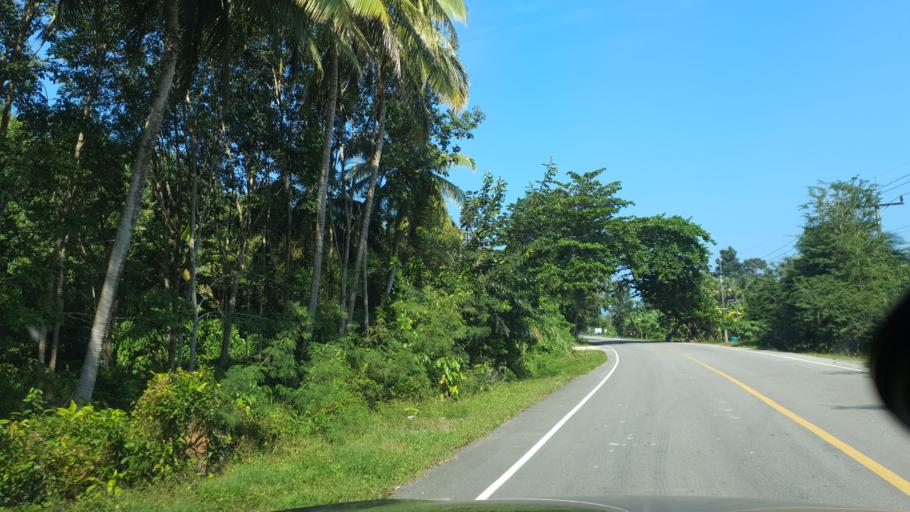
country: TH
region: Surat Thani
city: Tha Chana
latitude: 9.5842
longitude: 99.1984
